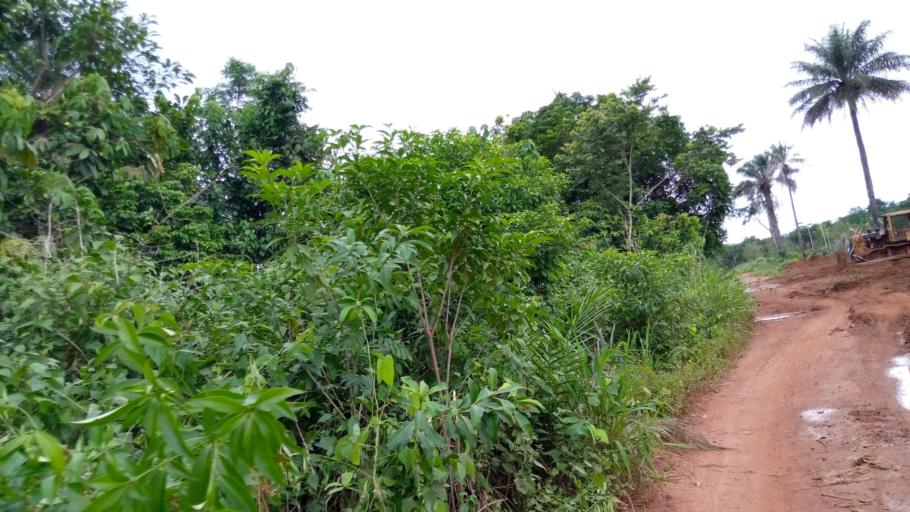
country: SL
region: Southern Province
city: Moyamba
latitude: 8.1955
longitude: -12.5438
